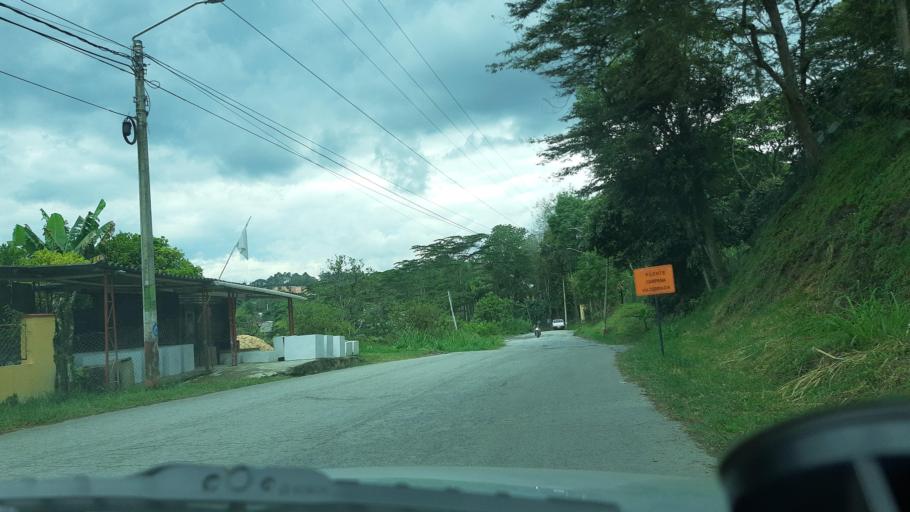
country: CO
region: Boyaca
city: Moniquira
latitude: 5.8840
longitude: -73.5772
